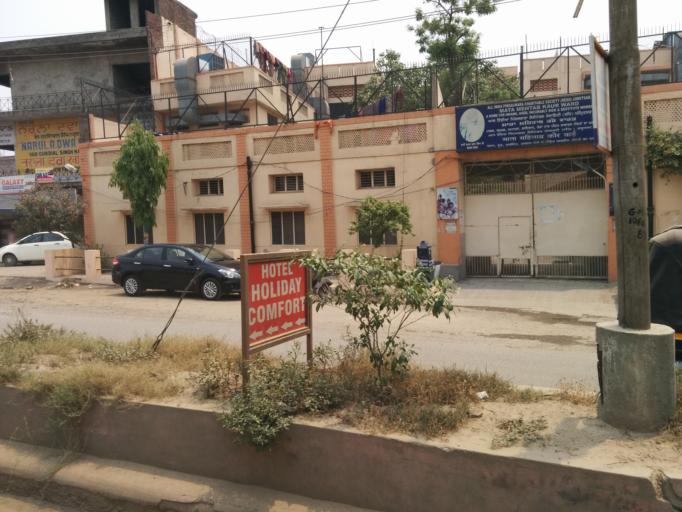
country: IN
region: Punjab
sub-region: Amritsar
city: Amritsar
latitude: 31.6276
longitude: 74.8880
